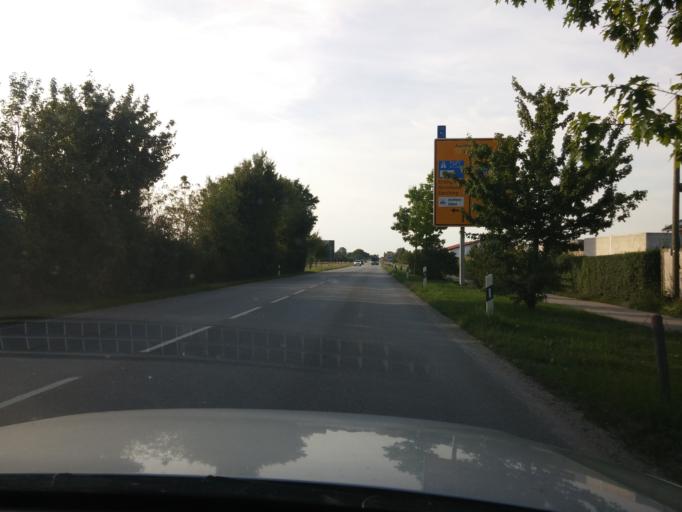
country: DE
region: Bavaria
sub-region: Upper Bavaria
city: Feldkirchen
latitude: 48.1543
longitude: 11.7248
